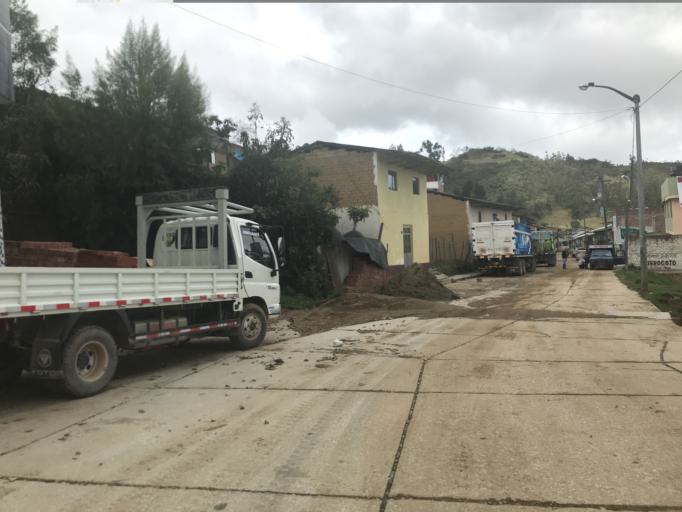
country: PE
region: Cajamarca
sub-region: Provincia de Chota
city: Querocoto
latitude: -6.3622
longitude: -79.0327
